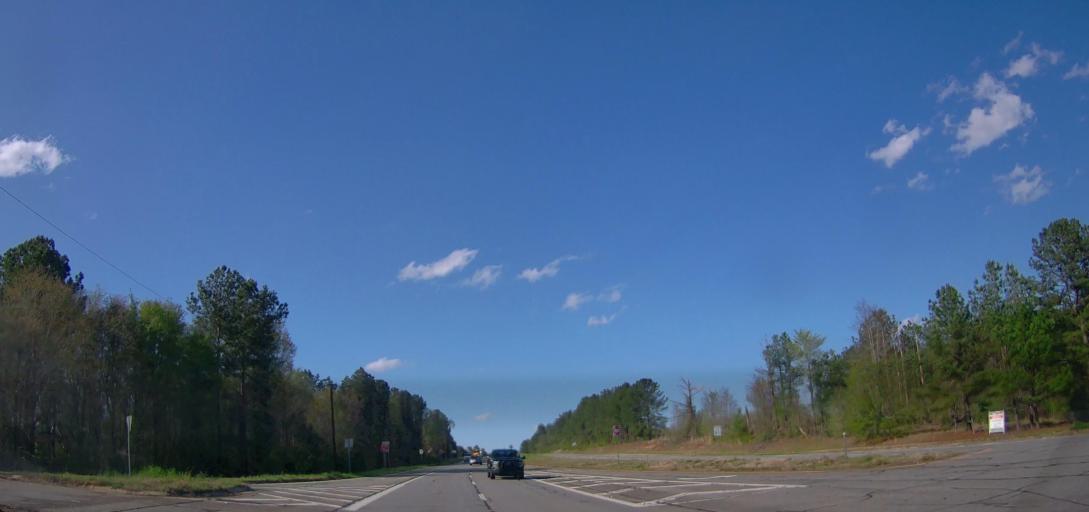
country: US
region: Georgia
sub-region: Baldwin County
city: Hardwick
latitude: 33.0443
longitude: -83.2557
